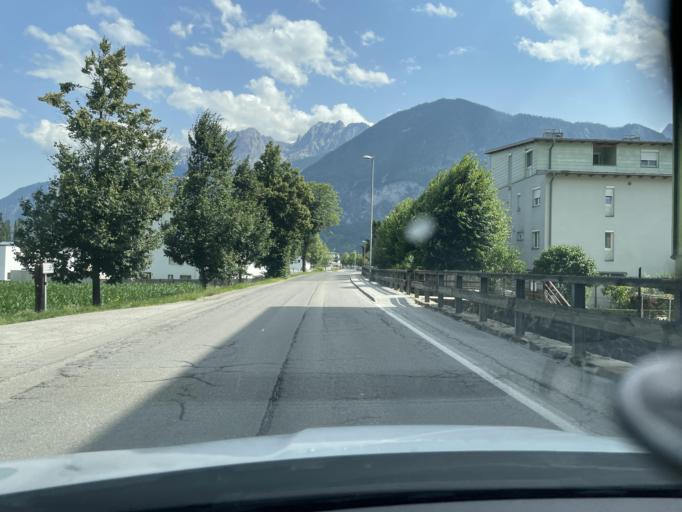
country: AT
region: Tyrol
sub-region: Politischer Bezirk Lienz
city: Lienz
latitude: 46.8345
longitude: 12.7775
